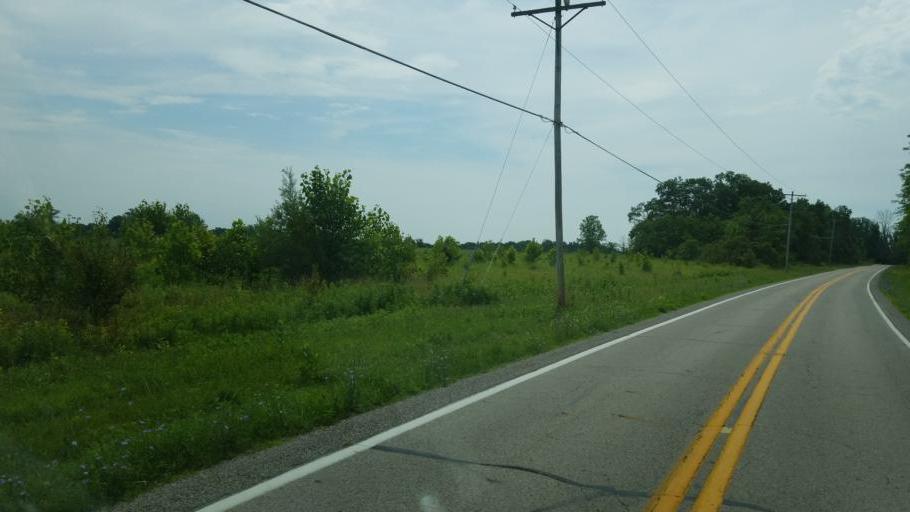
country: US
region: Ohio
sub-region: Franklin County
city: Lake Darby
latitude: 39.9031
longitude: -83.2290
